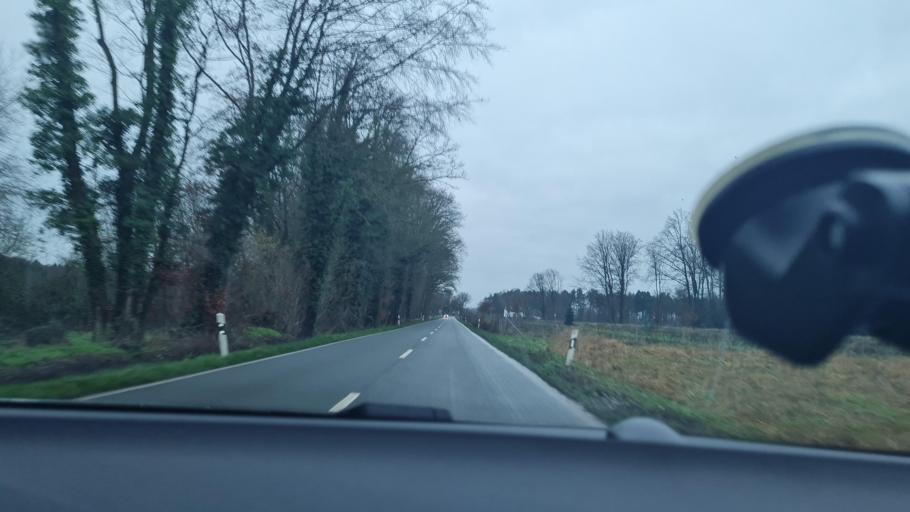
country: DE
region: North Rhine-Westphalia
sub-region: Regierungsbezirk Munster
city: Heiden
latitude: 51.7986
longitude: 6.9112
